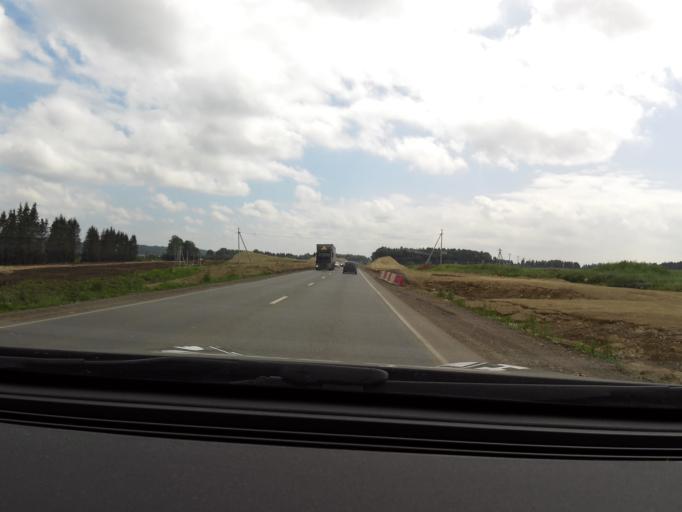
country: RU
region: Perm
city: Bershet'
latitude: 57.6854
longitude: 56.4169
